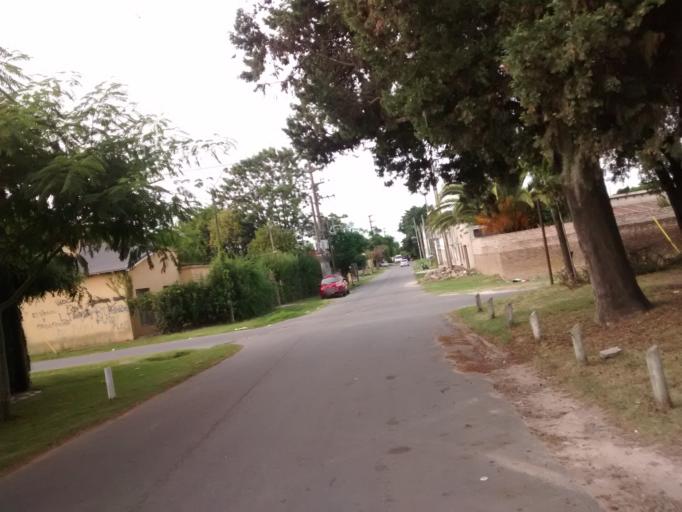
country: AR
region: Buenos Aires
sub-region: Partido de La Plata
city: La Plata
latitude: -34.8560
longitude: -58.0821
